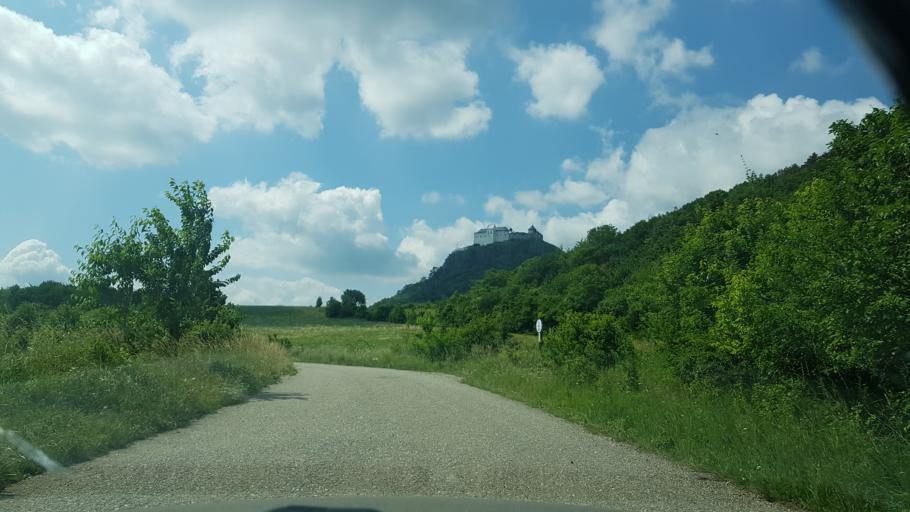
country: HU
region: Borsod-Abauj-Zemplen
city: Gonc
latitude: 48.5373
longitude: 21.4694
